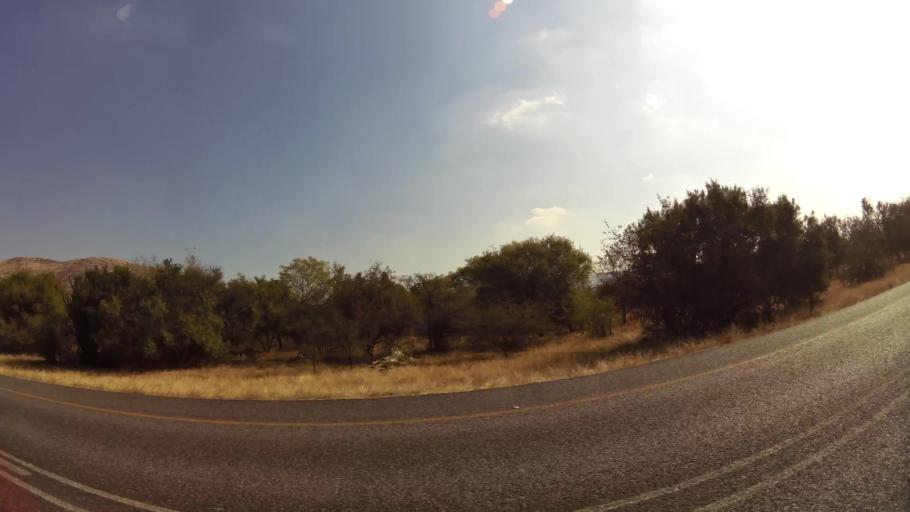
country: ZA
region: North-West
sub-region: Bojanala Platinum District Municipality
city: Rustenburg
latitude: -25.6321
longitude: 27.1573
